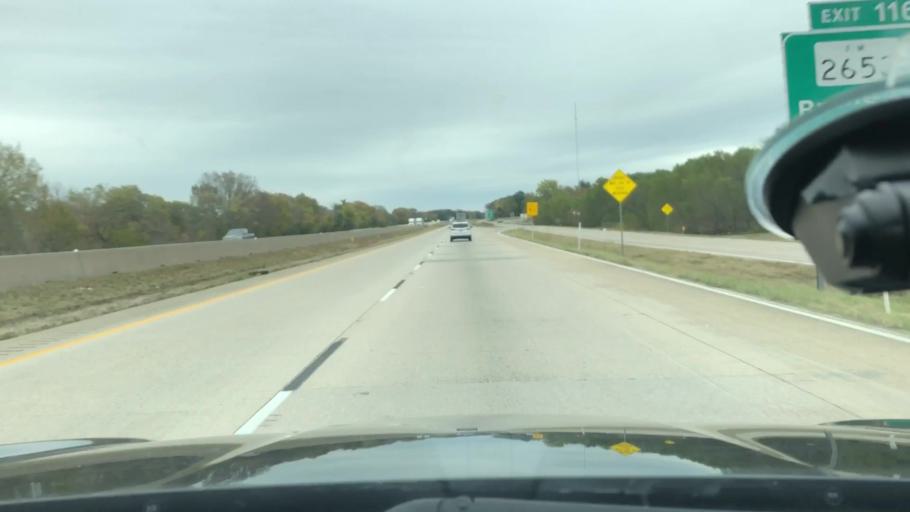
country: US
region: Texas
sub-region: Hopkins County
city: Sulphur Springs
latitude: 33.1275
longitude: -95.7525
